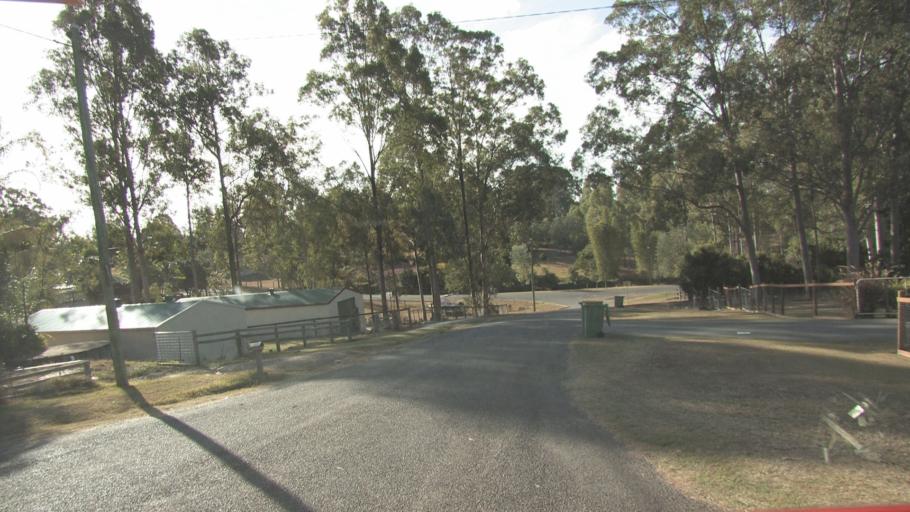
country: AU
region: Queensland
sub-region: Logan
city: Cedar Vale
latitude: -27.8745
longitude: 153.0052
